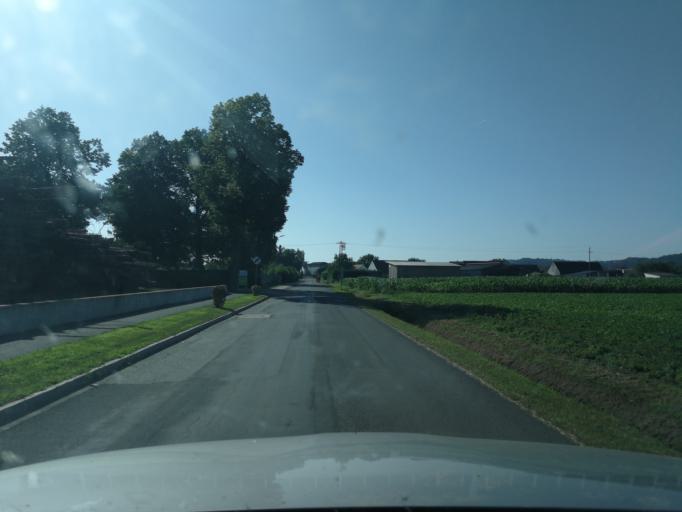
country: AT
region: Burgenland
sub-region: Politischer Bezirk Jennersdorf
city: Konigsdorf
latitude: 47.0065
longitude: 16.1637
